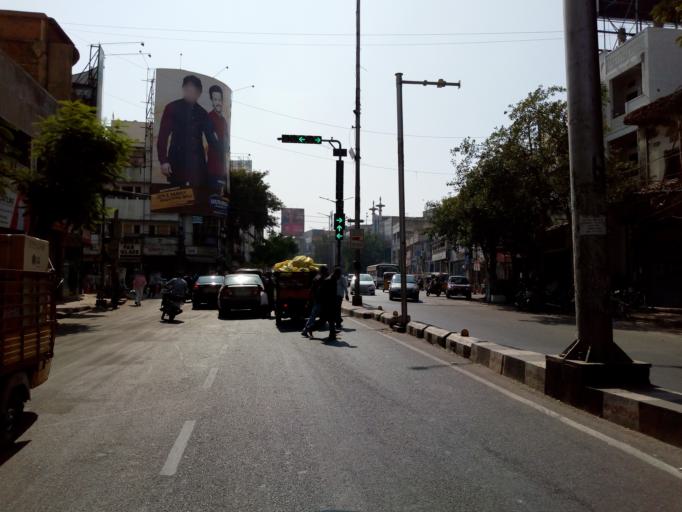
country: IN
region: Telangana
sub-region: Hyderabad
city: Malkajgiri
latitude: 17.4362
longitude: 78.4936
